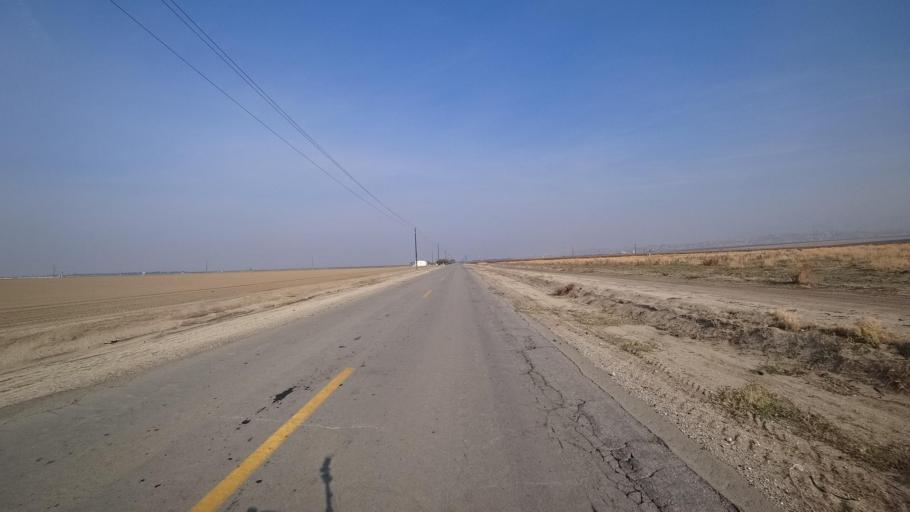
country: US
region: California
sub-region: Kern County
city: Arvin
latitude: 35.0721
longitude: -118.8467
